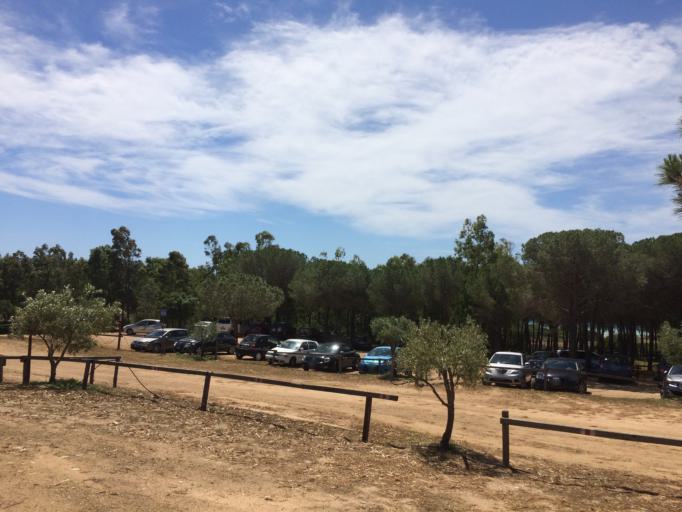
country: IT
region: Sardinia
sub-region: Provincia di Olbia-Tempio
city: San Teodoro
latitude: 40.8387
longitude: 9.6882
